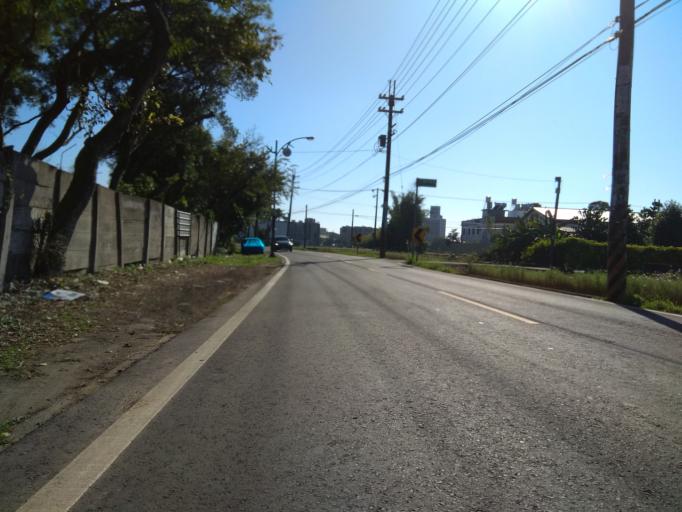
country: TW
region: Taiwan
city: Taoyuan City
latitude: 24.9901
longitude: 121.1936
